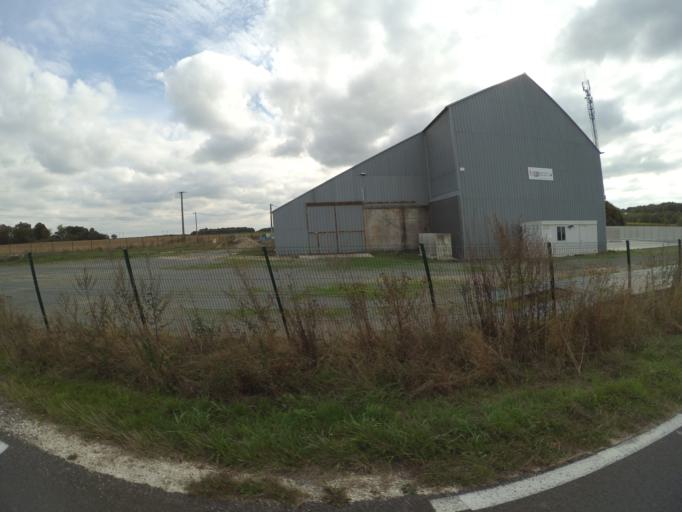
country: FR
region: Centre
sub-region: Departement d'Indre-et-Loire
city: Reugny
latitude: 47.4840
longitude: 0.9266
